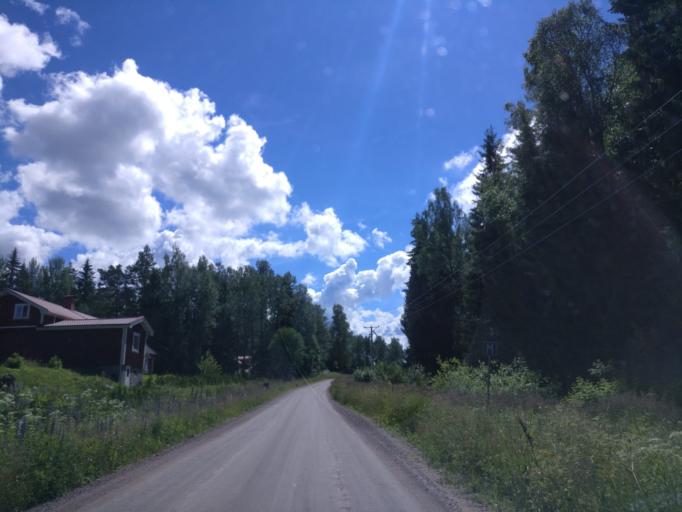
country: SE
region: Vaermland
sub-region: Hagfors Kommun
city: Hagfors
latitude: 60.0359
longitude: 13.6672
